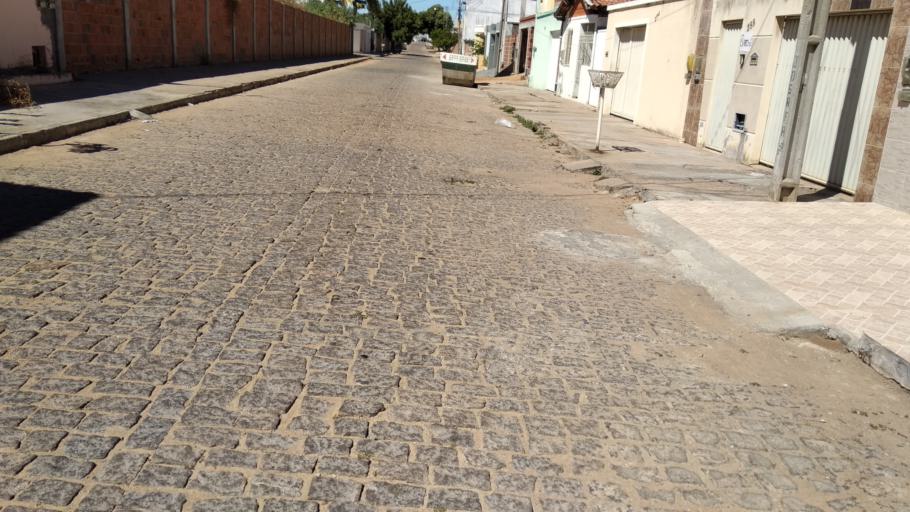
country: BR
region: Bahia
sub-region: Guanambi
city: Guanambi
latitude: -14.2363
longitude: -42.7741
